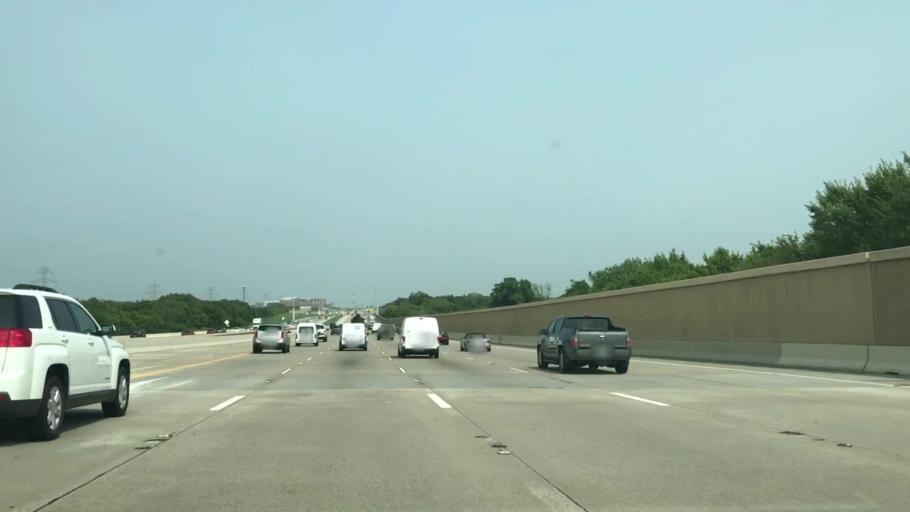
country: US
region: Texas
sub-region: Dallas County
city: Addison
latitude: 33.0125
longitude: -96.8186
